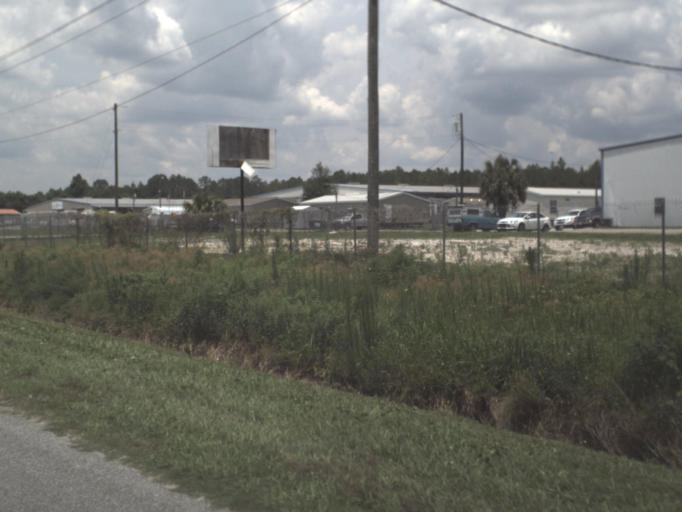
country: US
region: Florida
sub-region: Columbia County
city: Watertown
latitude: 30.1689
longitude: -82.5787
